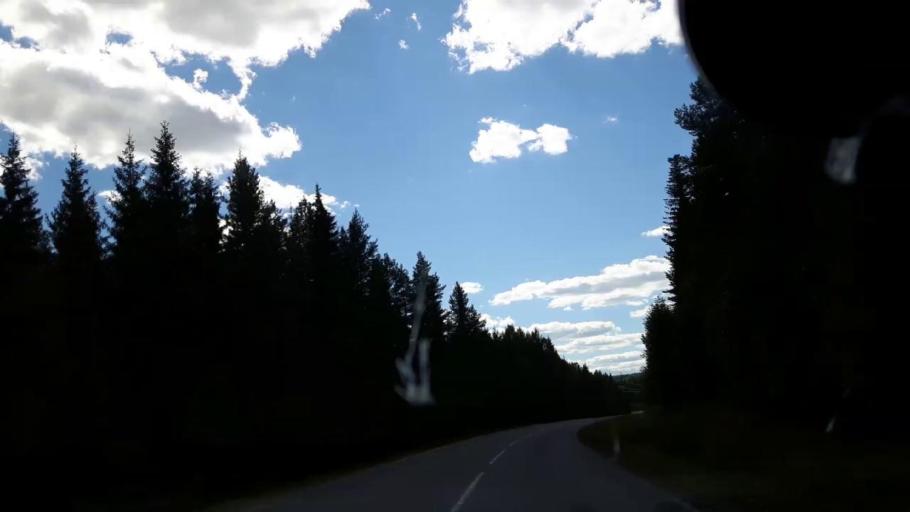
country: SE
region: Jaemtland
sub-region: Ragunda Kommun
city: Hammarstrand
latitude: 62.8515
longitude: 16.1849
